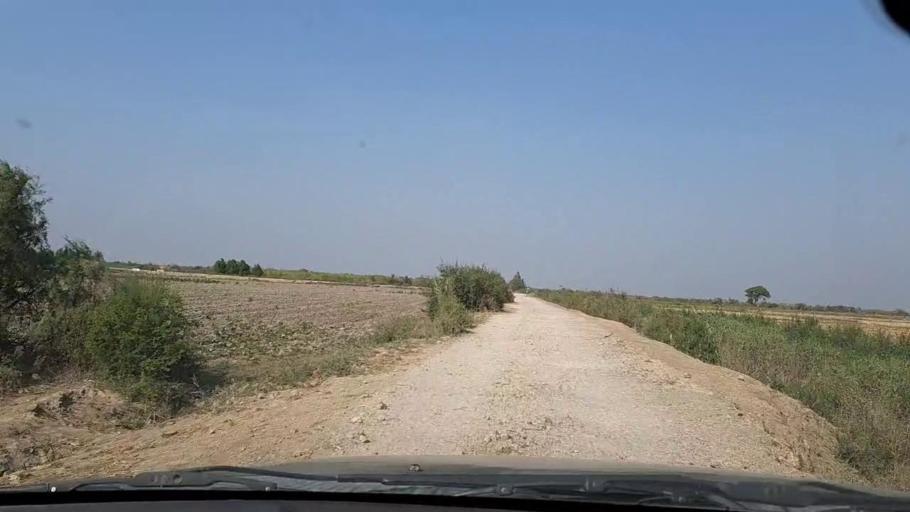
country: PK
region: Sindh
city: Mirpur Sakro
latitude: 24.3754
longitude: 67.6829
